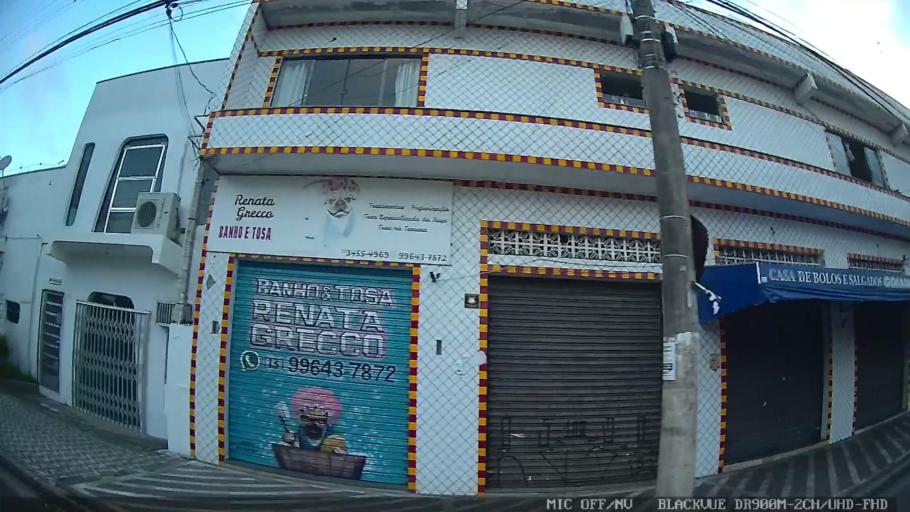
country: BR
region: Sao Paulo
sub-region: Peruibe
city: Peruibe
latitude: -24.3227
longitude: -47.0010
